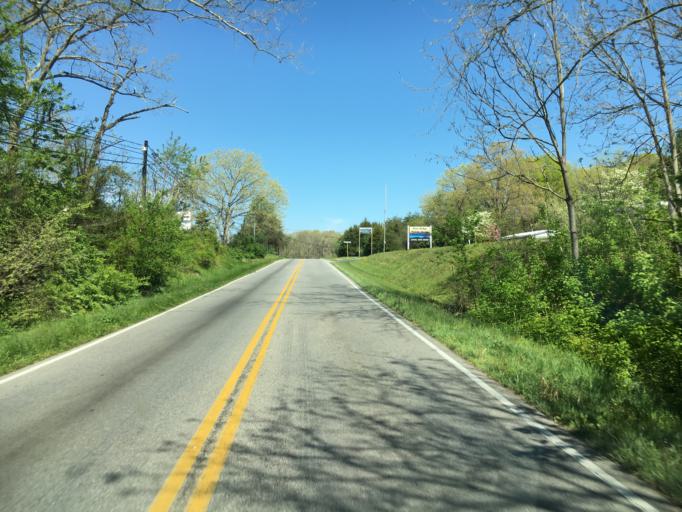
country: US
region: Virginia
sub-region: Augusta County
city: Crimora
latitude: 38.1593
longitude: -78.8471
